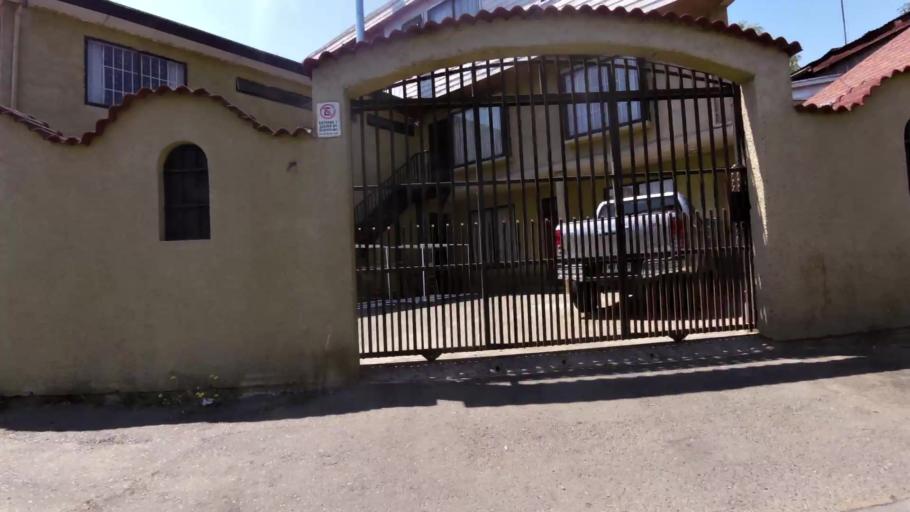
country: CL
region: Biobio
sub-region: Provincia de Concepcion
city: Concepcion
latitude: -36.8039
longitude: -73.0557
